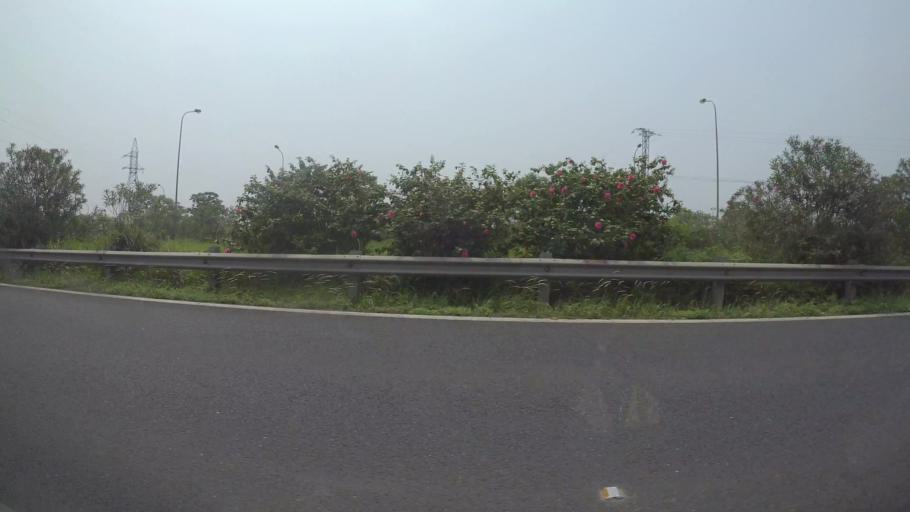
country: VN
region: Ha Noi
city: Quoc Oai
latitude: 21.0024
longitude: 105.6270
